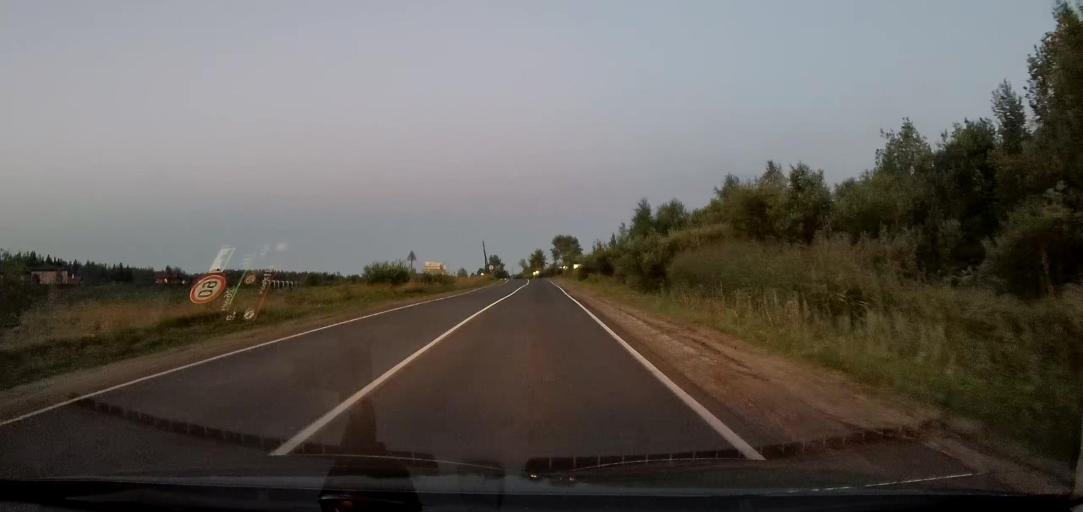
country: RU
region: Arkhangelskaya
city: Uyemskiy
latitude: 64.4484
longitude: 40.9455
